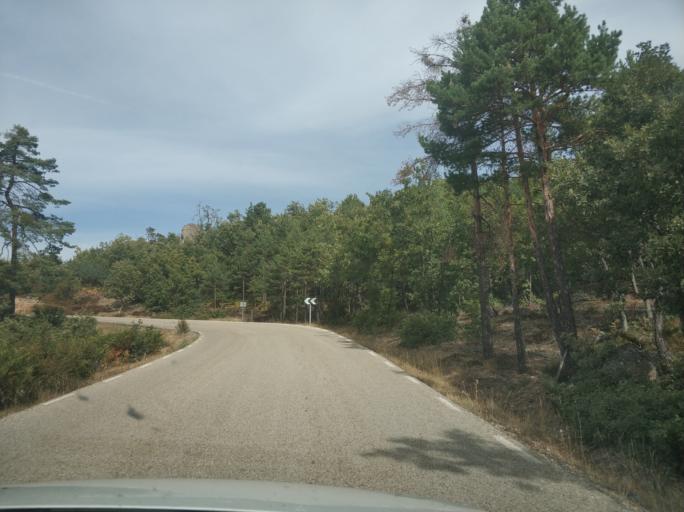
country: ES
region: Castille and Leon
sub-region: Provincia de Soria
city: Duruelo de la Sierra
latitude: 41.9076
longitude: -2.9444
